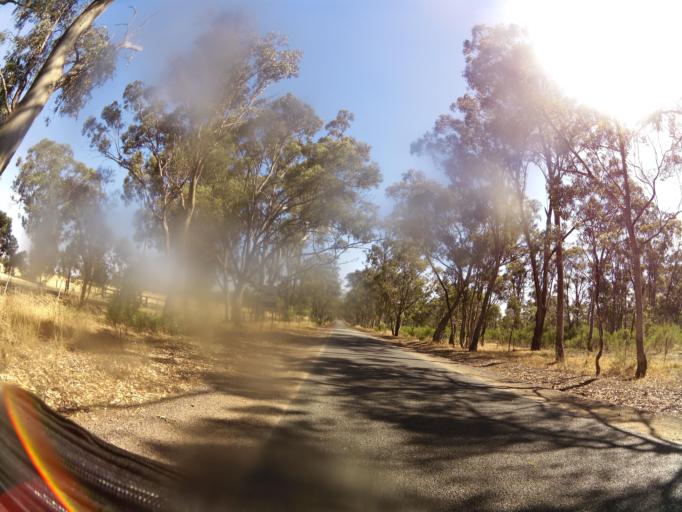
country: AU
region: Victoria
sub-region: Campaspe
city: Kyabram
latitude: -36.8733
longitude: 145.0860
